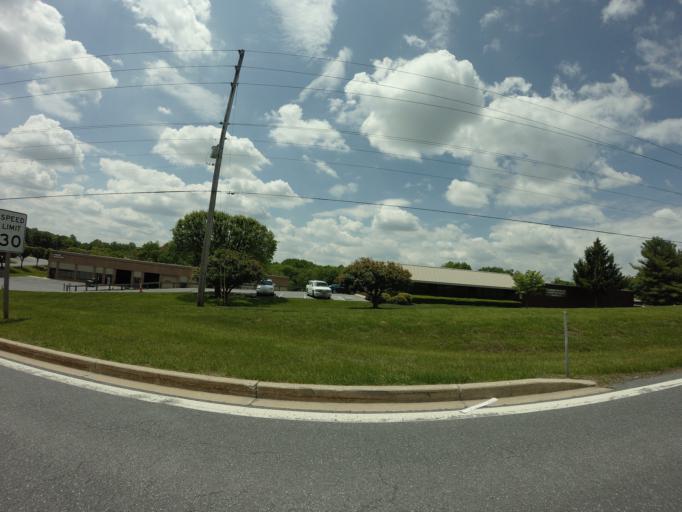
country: US
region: Maryland
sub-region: Frederick County
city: Green Valley
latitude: 39.2921
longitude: -77.3147
